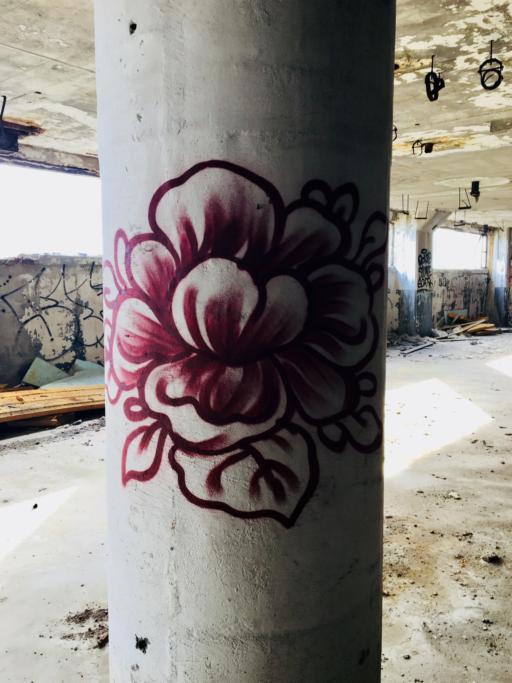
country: US
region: Michigan
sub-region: Wayne County
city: Hamtramck
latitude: 42.3684
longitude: -83.0492
